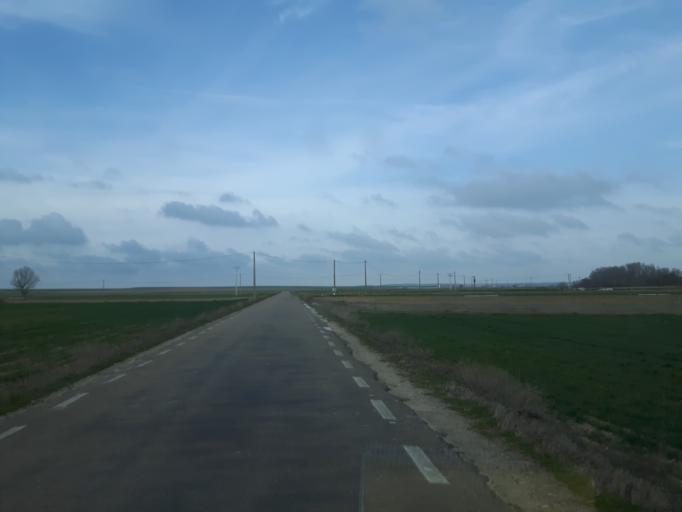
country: ES
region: Castille and Leon
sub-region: Provincia de Salamanca
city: Tordillos
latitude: 40.8602
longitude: -5.3614
